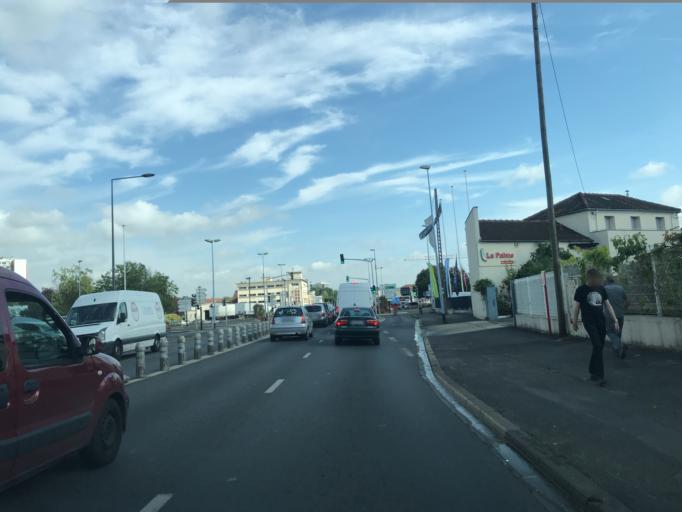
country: FR
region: Ile-de-France
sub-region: Departement de Seine-Saint-Denis
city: Pantin
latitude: 48.9069
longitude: 2.4244
